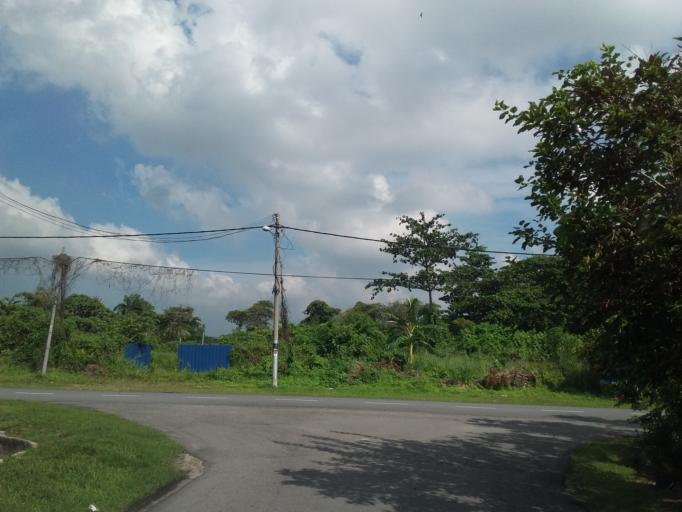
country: MY
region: Johor
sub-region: Daerah Batu Pahat
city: Batu Pahat
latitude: 1.8409
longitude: 102.9254
